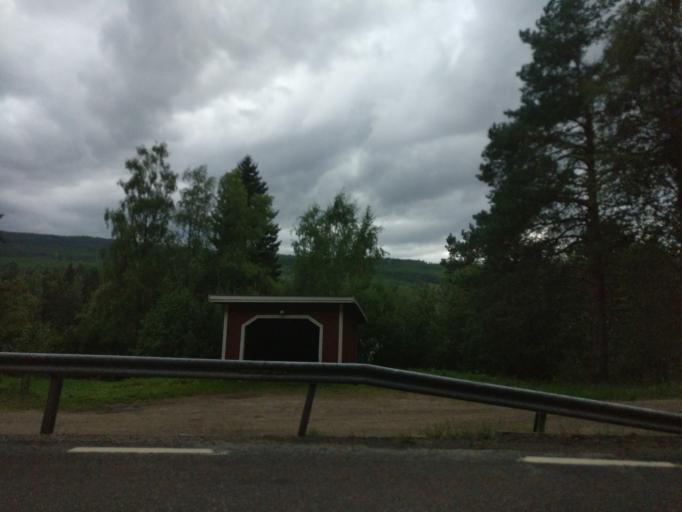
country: SE
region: Vaermland
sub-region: Torsby Kommun
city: Torsby
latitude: 60.6234
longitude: 13.0319
